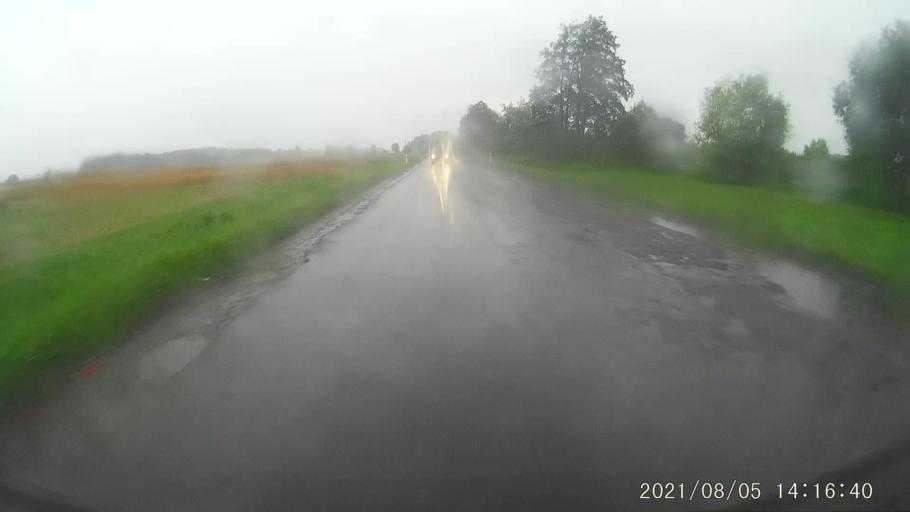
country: PL
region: Opole Voivodeship
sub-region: Powiat prudnicki
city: Biala
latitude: 50.4593
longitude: 17.7185
